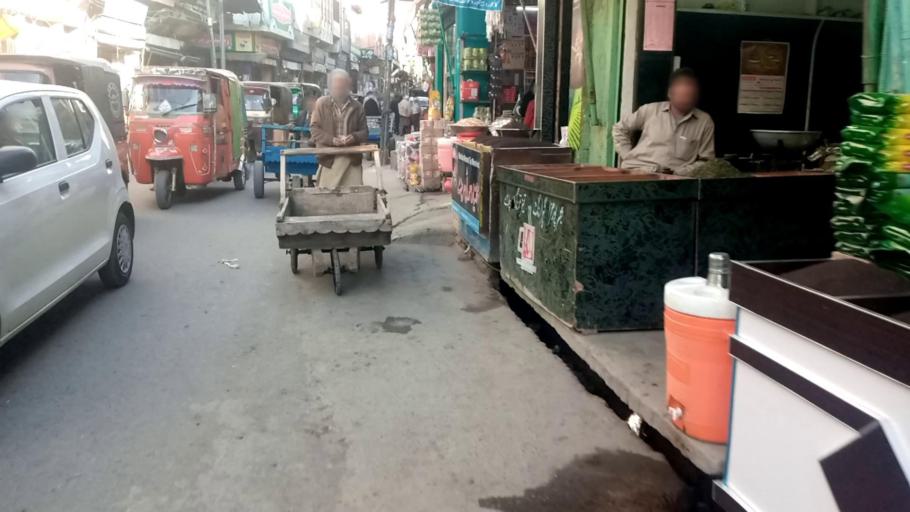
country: PK
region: Khyber Pakhtunkhwa
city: Mingora
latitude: 34.7762
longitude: 72.3588
